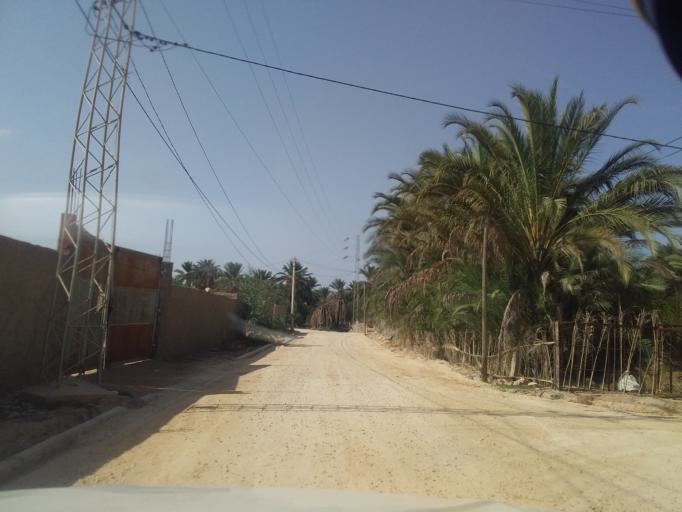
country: TN
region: Qabis
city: Gabes
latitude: 33.6249
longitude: 10.2844
